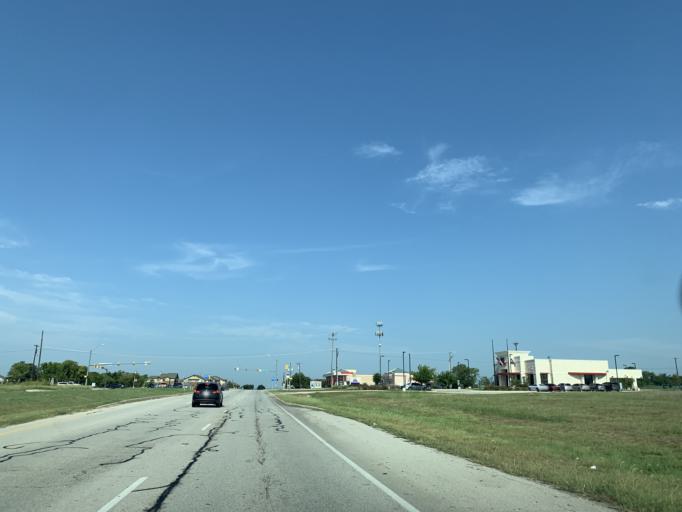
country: US
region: Texas
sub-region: Tarrant County
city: Blue Mound
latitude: 32.8962
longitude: -97.3052
